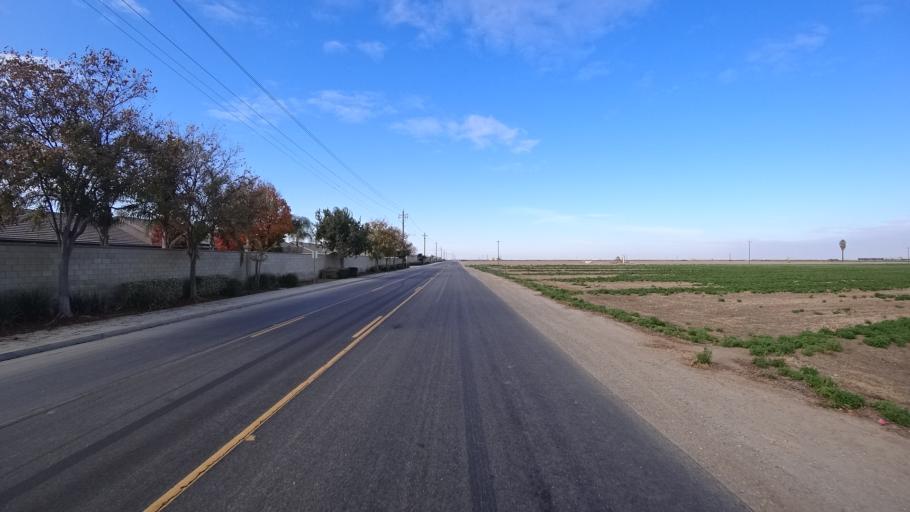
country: US
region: California
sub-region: Kern County
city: Rosedale
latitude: 35.3034
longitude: -119.1396
